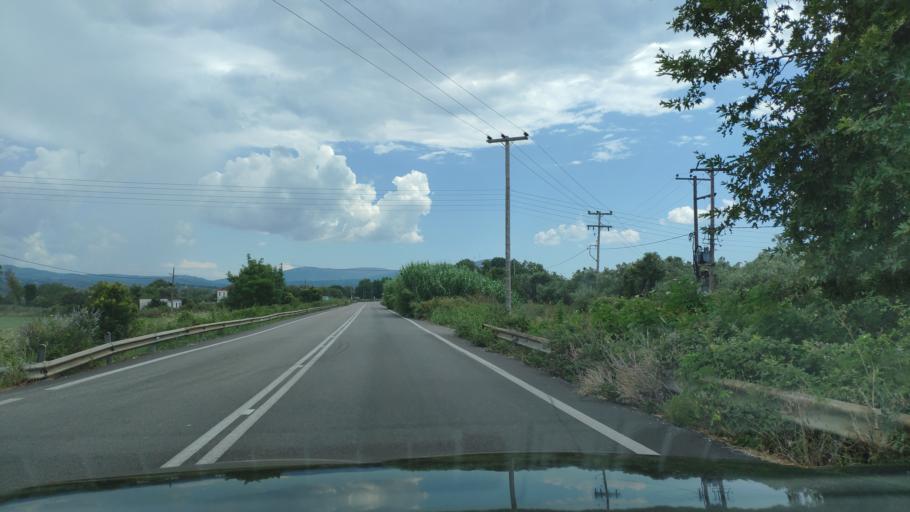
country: GR
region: West Greece
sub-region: Nomos Aitolias kai Akarnanias
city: Krikellos
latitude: 38.9226
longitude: 21.1780
